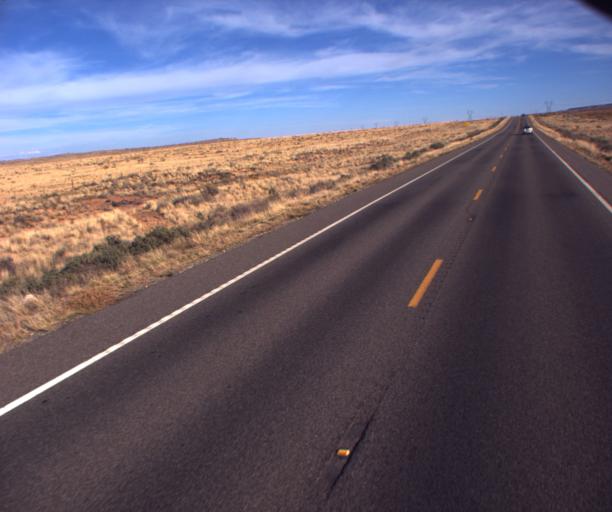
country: US
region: Arizona
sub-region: Apache County
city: Lukachukai
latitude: 36.9405
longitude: -109.2511
